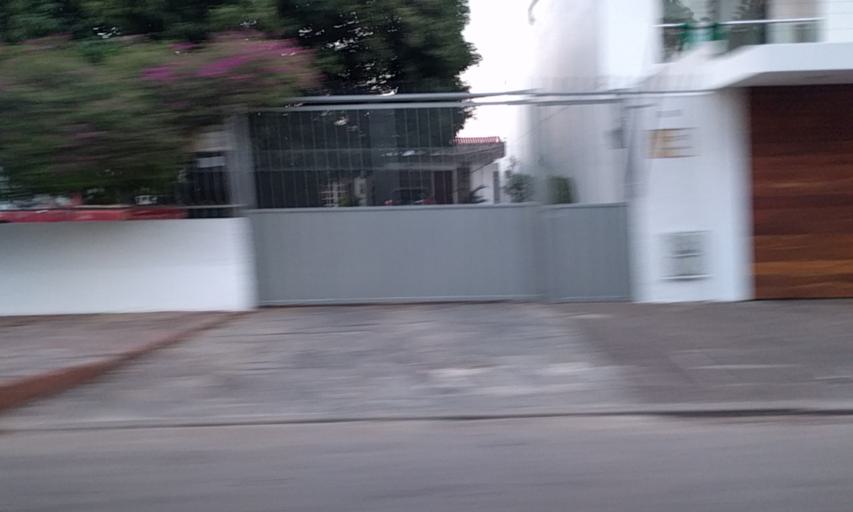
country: BO
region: Santa Cruz
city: Santa Cruz de la Sierra
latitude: -17.7657
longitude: -63.1702
